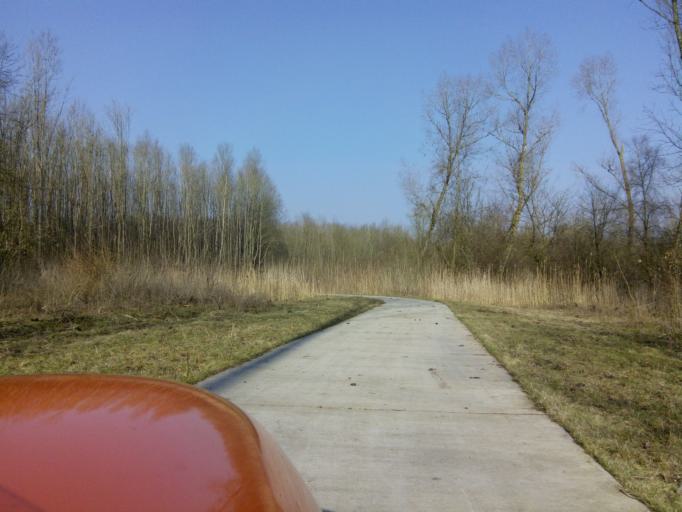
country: NL
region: Gelderland
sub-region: Gemeente Nijkerk
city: Nijkerk
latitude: 52.2859
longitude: 5.4636
